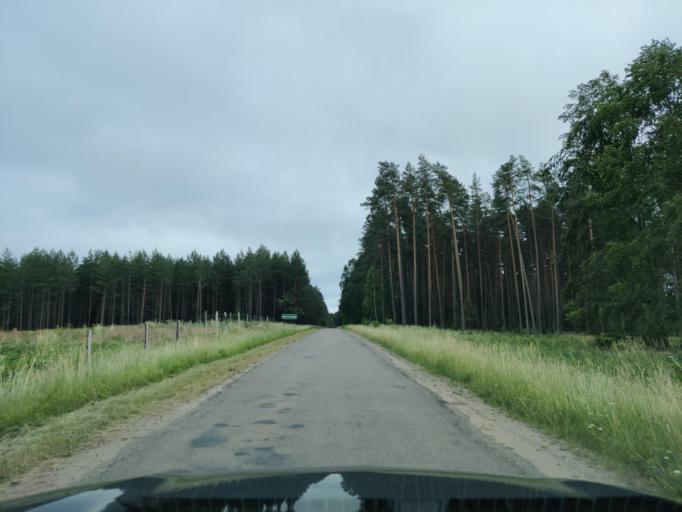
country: PL
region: Warmian-Masurian Voivodeship
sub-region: Powiat piski
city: Ruciane-Nida
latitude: 53.6156
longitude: 21.4442
